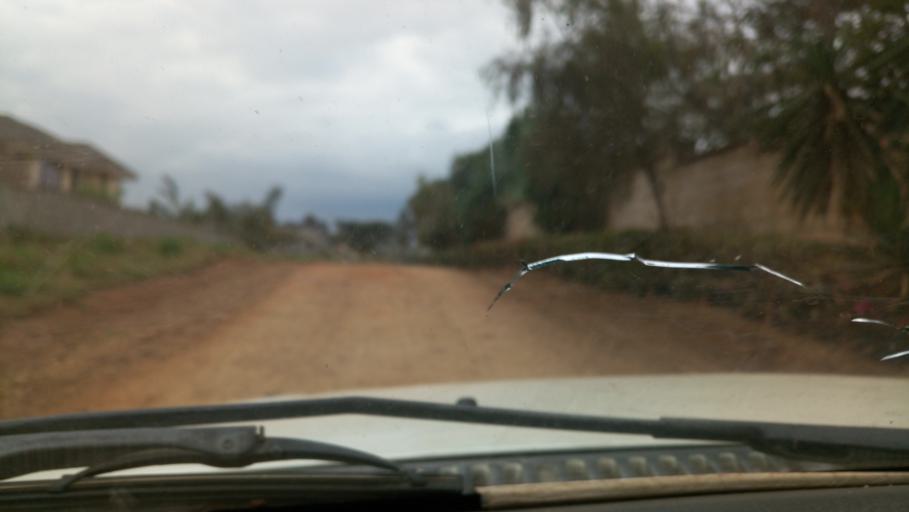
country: KE
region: Nairobi Area
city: Pumwani
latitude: -1.2296
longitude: 36.8593
